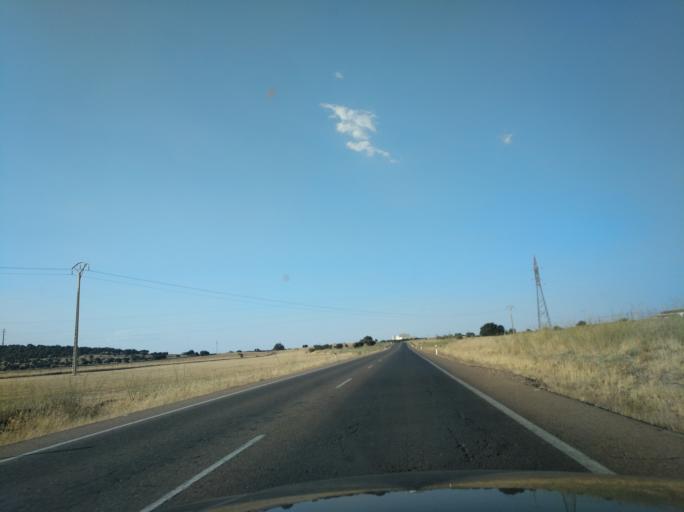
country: ES
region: Extremadura
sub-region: Provincia de Badajoz
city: Olivenza
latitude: 38.7007
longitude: -7.0887
